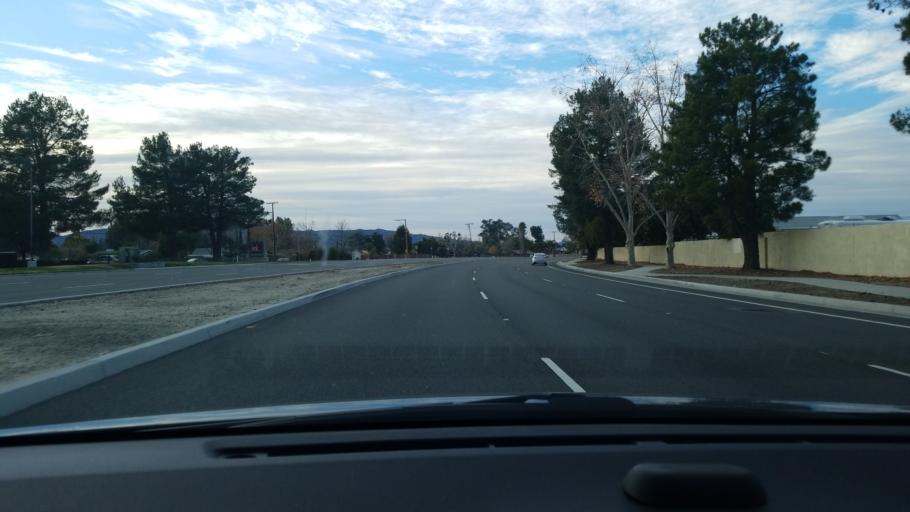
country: US
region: California
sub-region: Riverside County
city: San Jacinto
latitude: 33.8021
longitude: -116.9736
